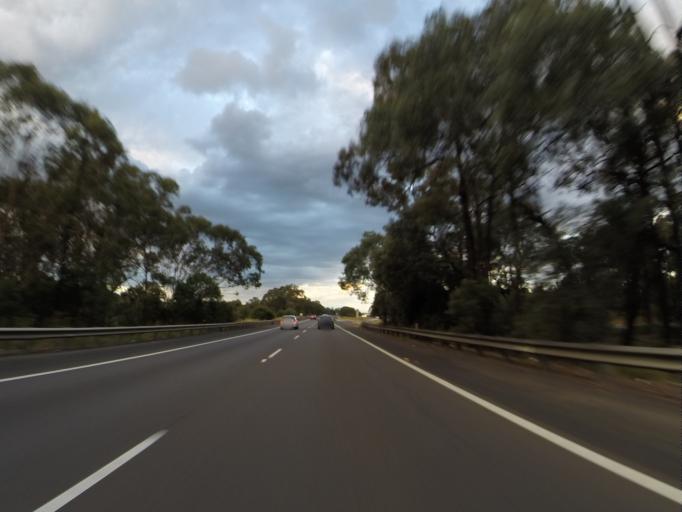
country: AU
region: New South Wales
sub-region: Wollondilly
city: Douglas Park
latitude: -34.1895
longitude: 150.7142
